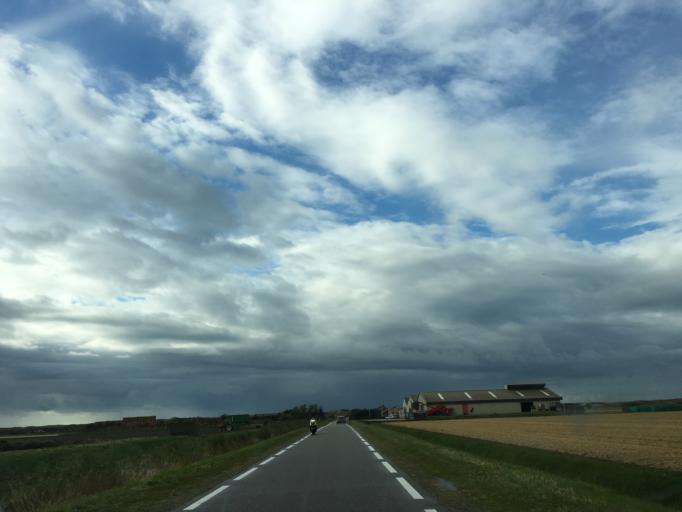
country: NL
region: North Holland
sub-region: Gemeente Den Helder
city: Den Helder
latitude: 52.9148
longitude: 4.7402
